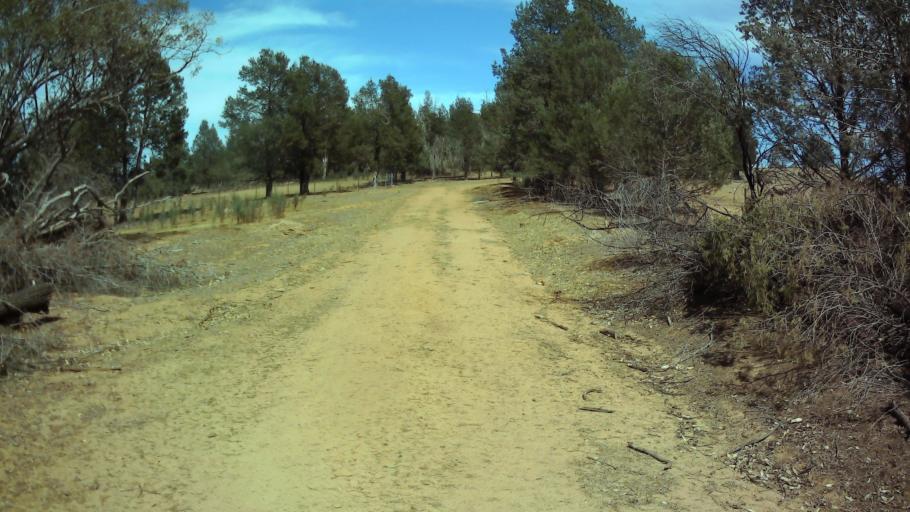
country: AU
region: New South Wales
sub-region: Weddin
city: Grenfell
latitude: -33.6793
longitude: 148.2607
